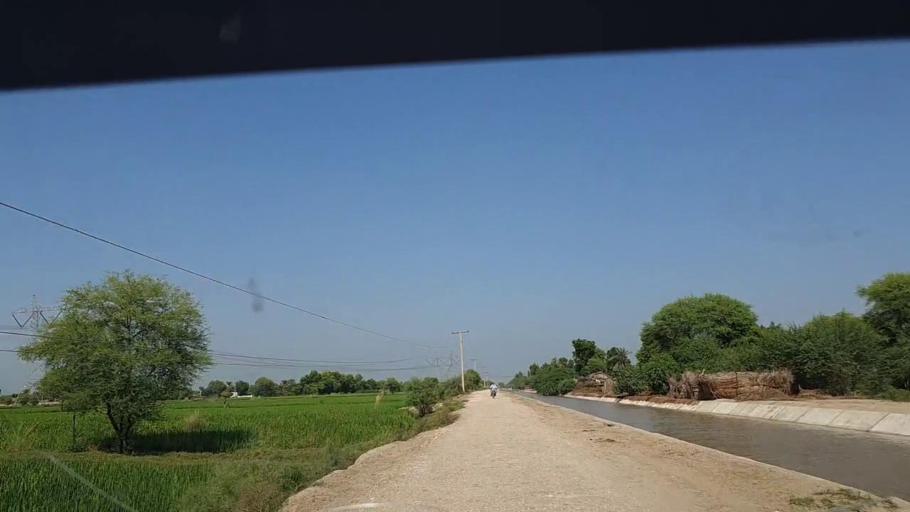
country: PK
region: Sindh
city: Ghauspur
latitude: 28.1511
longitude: 69.0804
